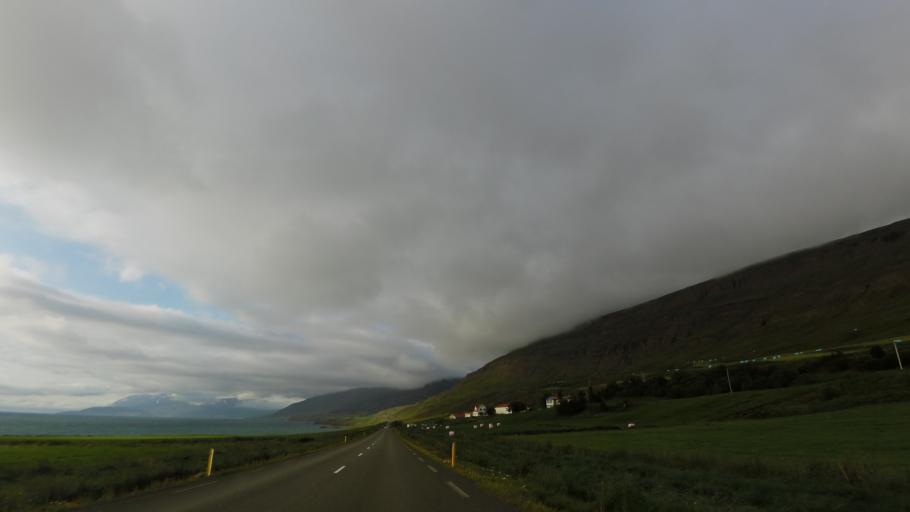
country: IS
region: Northeast
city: Akureyri
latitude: 65.7827
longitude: -18.0654
